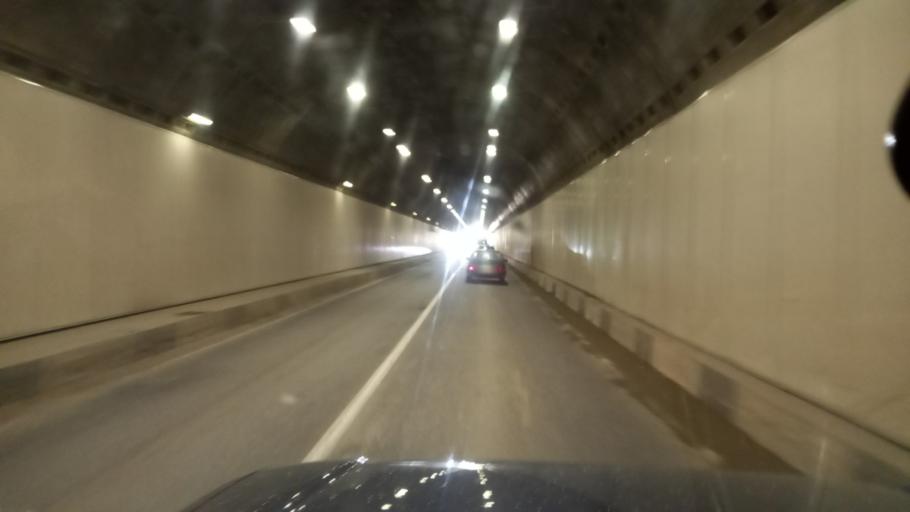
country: RU
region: Dagestan
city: Derbent
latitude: 42.0554
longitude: 48.2783
